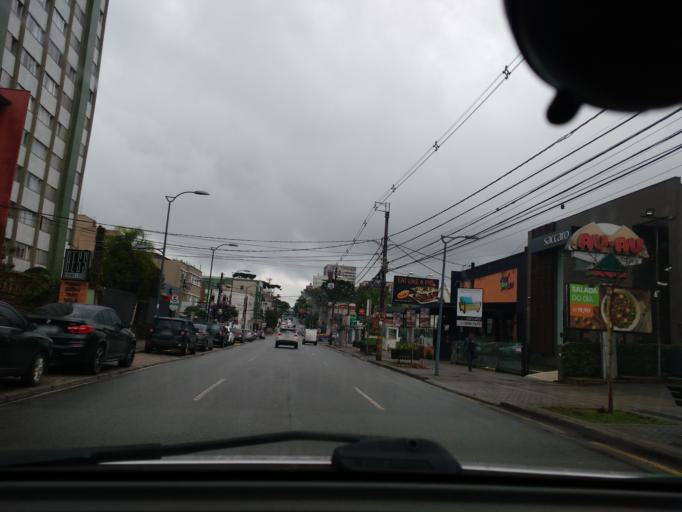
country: BR
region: Parana
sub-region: Curitiba
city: Curitiba
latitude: -25.4348
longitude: -49.2844
